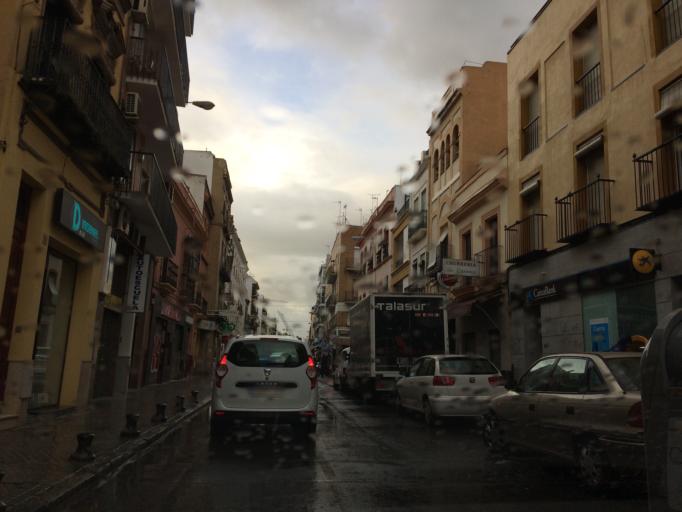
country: ES
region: Andalusia
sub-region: Provincia de Sevilla
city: Sevilla
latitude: 37.3997
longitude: -5.9917
